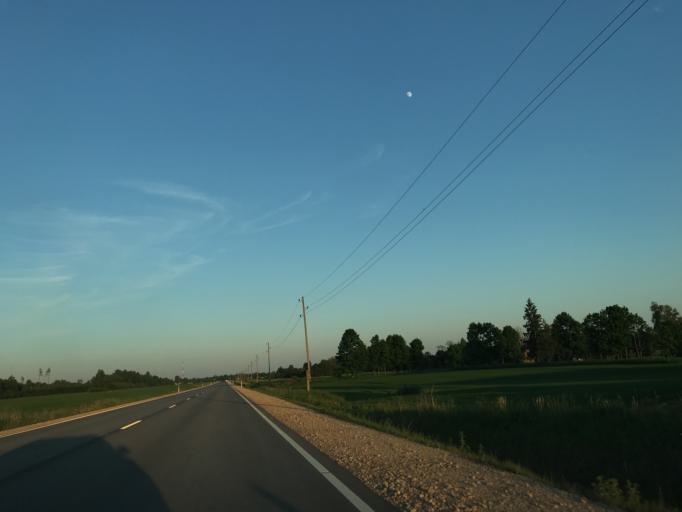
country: LV
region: Jaunjelgava
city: Jaunjelgava
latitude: 56.3841
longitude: 24.9795
